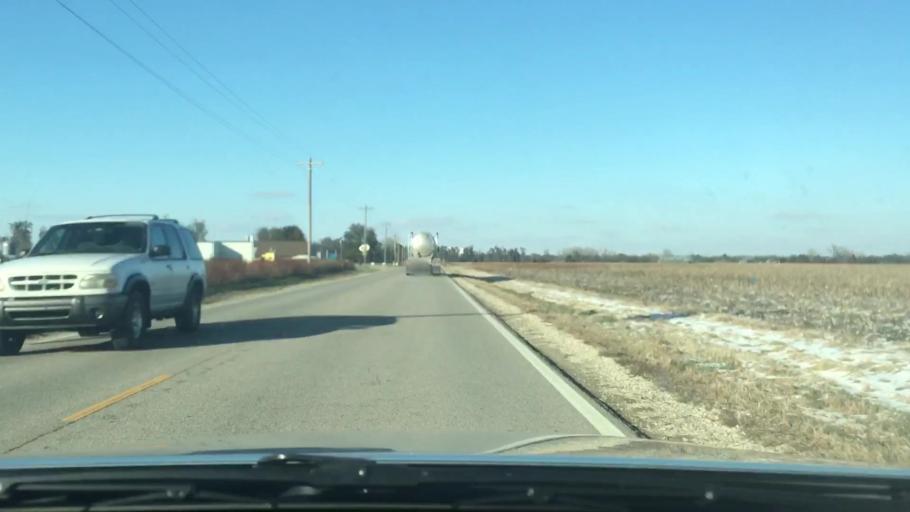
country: US
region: Kansas
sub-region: Rice County
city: Sterling
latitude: 38.1847
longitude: -98.2068
